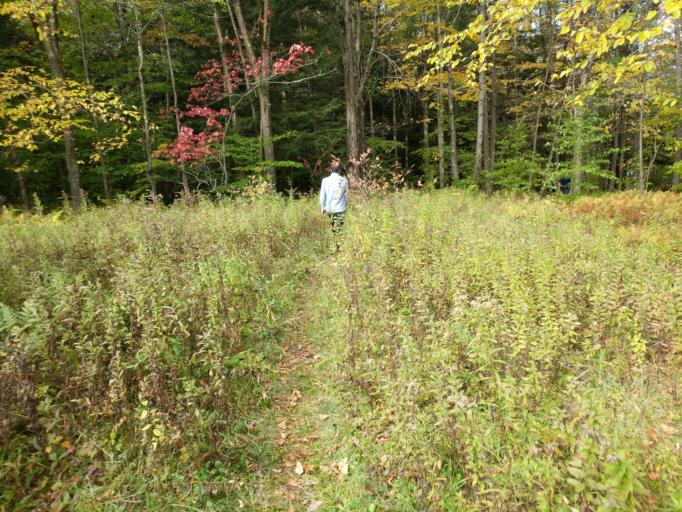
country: US
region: New York
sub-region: Sullivan County
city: Livingston Manor
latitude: 41.8718
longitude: -75.0284
